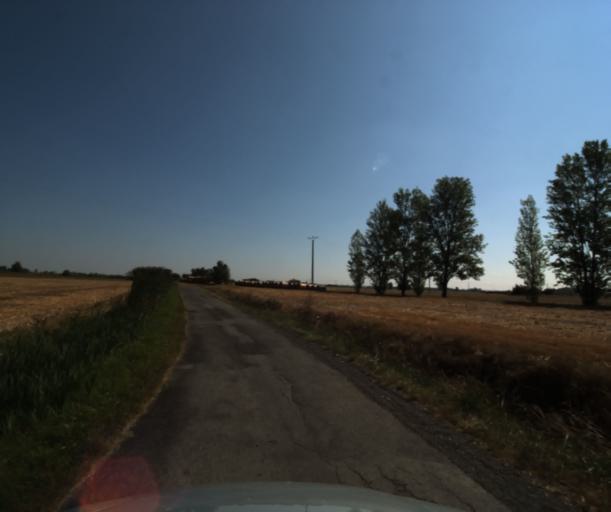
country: FR
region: Midi-Pyrenees
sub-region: Departement de la Haute-Garonne
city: Labastidette
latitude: 43.4417
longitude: 1.2423
